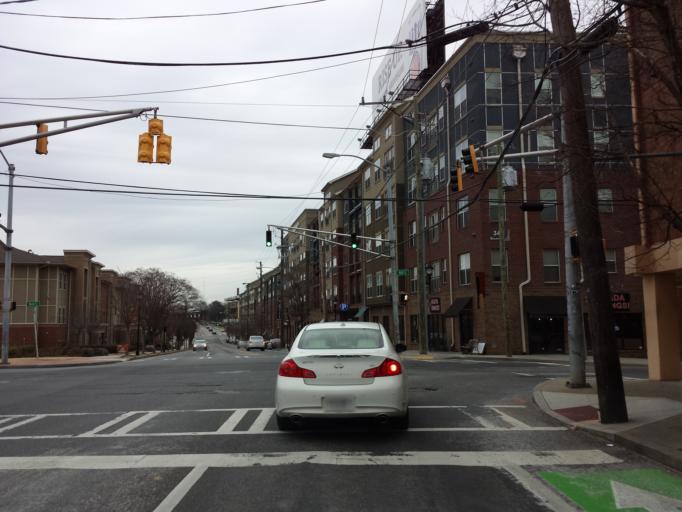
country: US
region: Georgia
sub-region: Fulton County
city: Atlanta
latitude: 33.7498
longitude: -84.3798
